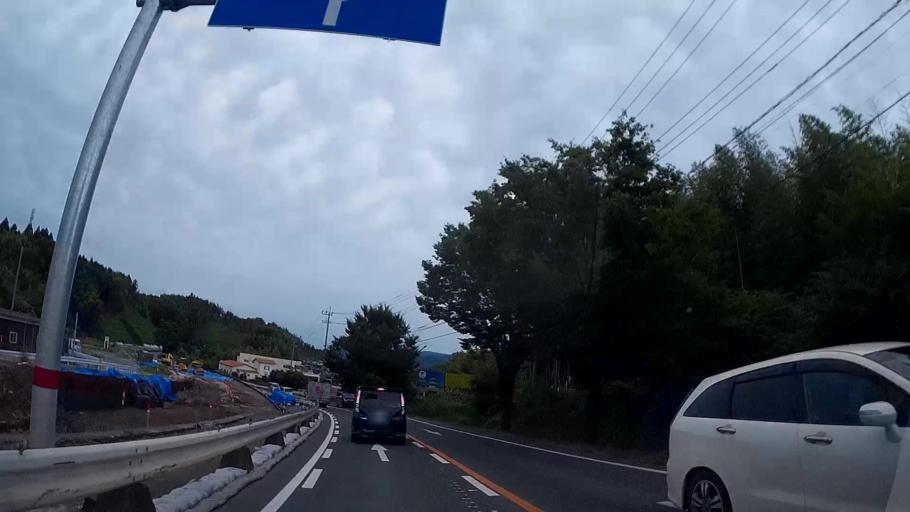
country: JP
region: Kumamoto
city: Kikuchi
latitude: 32.9519
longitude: 130.8242
